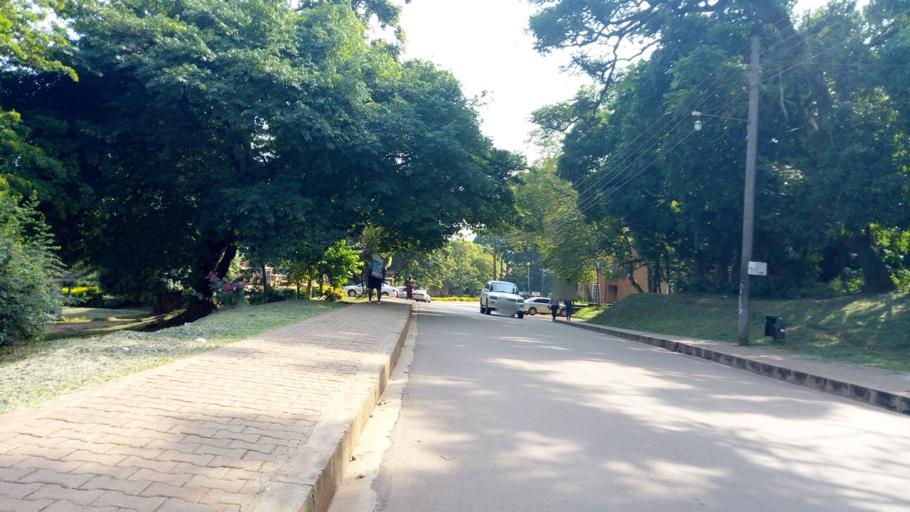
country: UG
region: Central Region
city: Kampala Central Division
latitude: 0.3303
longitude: 32.5690
